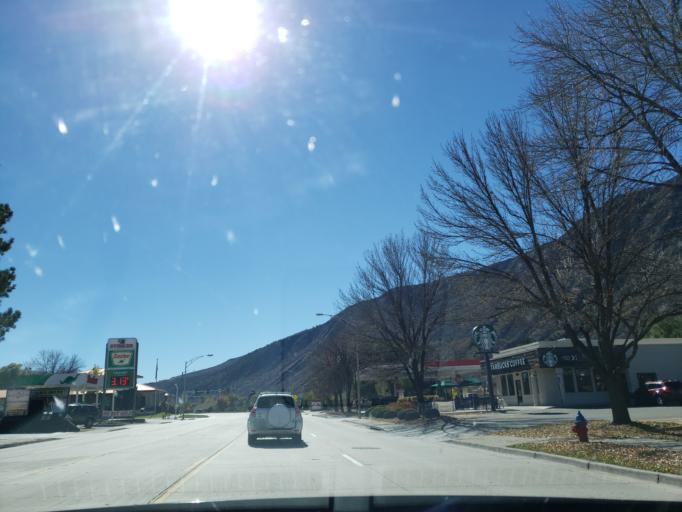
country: US
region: Colorado
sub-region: Garfield County
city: Glenwood Springs
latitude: 39.5312
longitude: -107.3253
